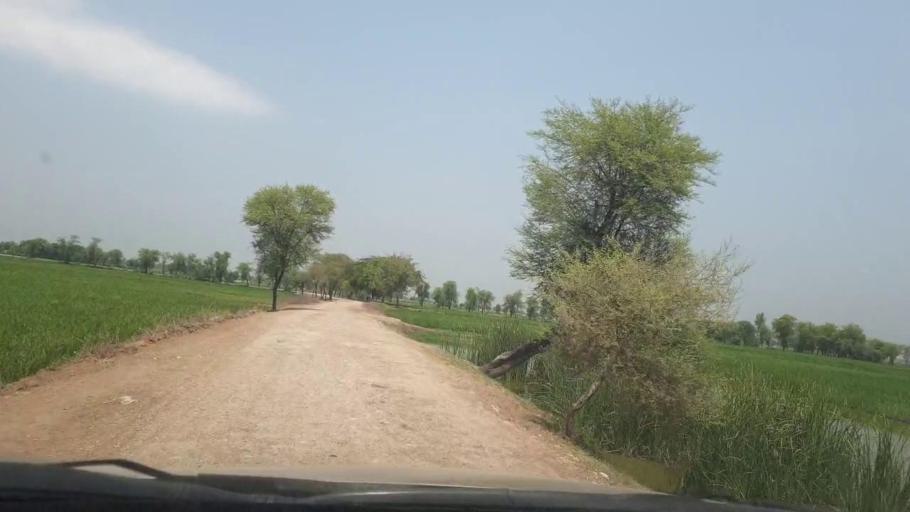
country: PK
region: Sindh
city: Ratodero
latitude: 27.7321
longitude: 68.2968
